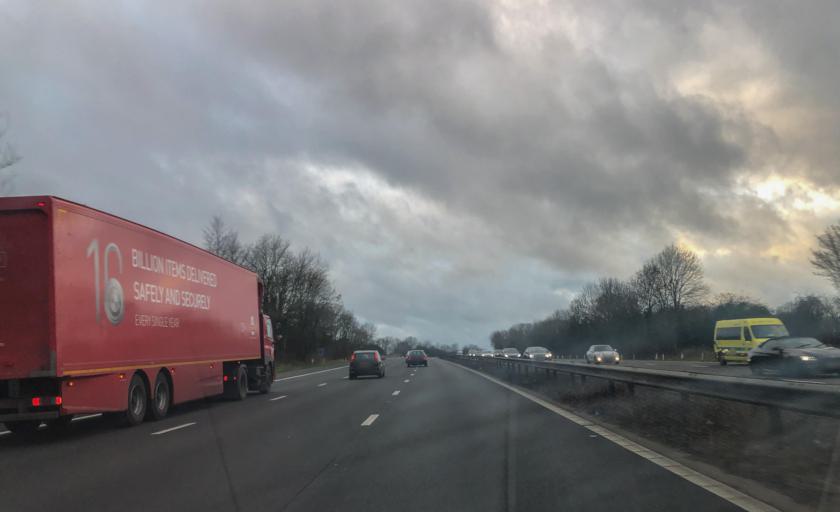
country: GB
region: England
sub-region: Buckinghamshire
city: High Wycombe
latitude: 51.6104
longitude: -0.7218
